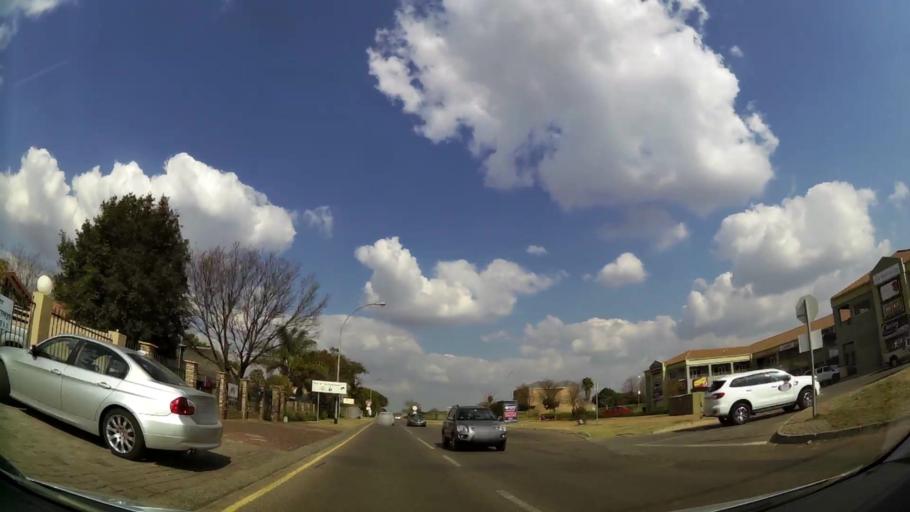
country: ZA
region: Gauteng
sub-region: City of Tshwane Metropolitan Municipality
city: Centurion
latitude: -25.8417
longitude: 28.2442
